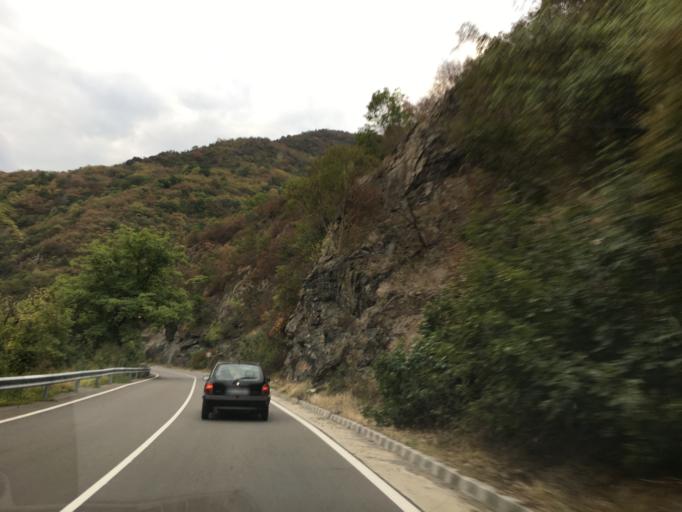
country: BG
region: Sofiya
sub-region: Obshtina Svoge
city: Bov
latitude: 43.0439
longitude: 23.3531
